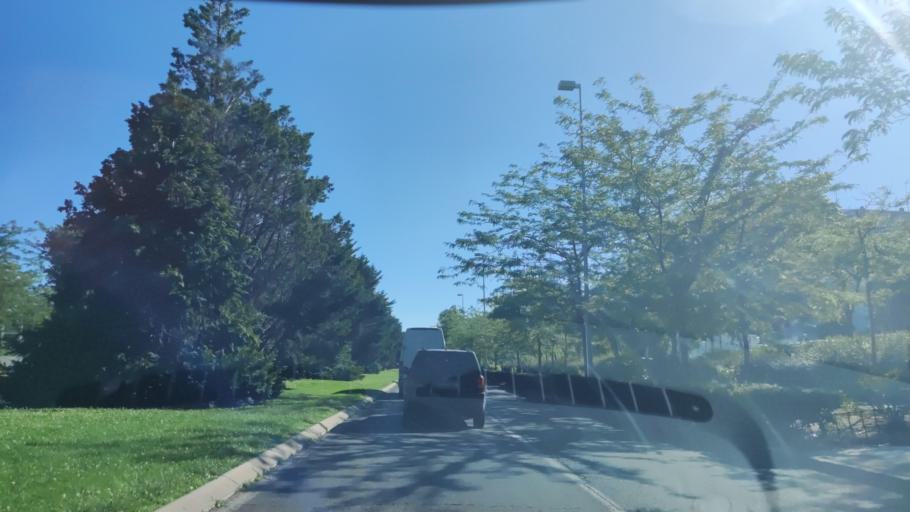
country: ES
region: Madrid
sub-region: Provincia de Madrid
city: Carabanchel
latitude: 40.3785
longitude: -3.7283
